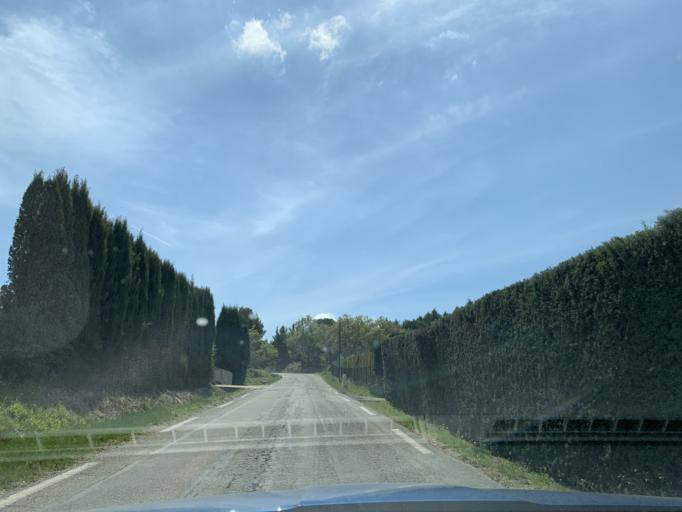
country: FR
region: Provence-Alpes-Cote d'Azur
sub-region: Departement du Vaucluse
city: Saint-Didier
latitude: 44.0003
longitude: 5.1067
